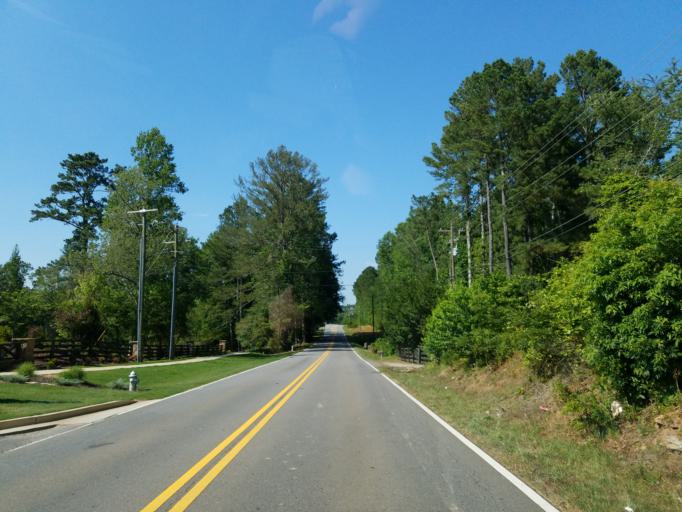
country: US
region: Georgia
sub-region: Fulton County
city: Milton
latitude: 34.1760
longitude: -84.3265
